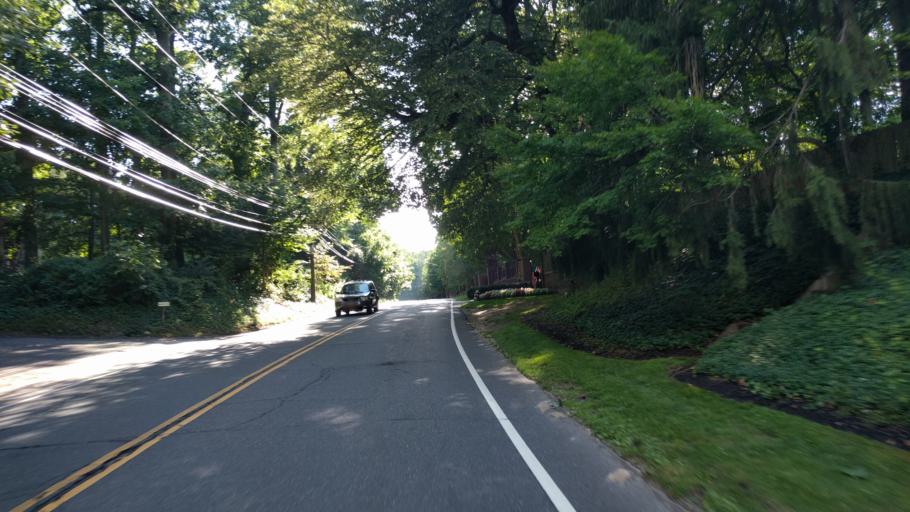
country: US
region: New York
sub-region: Nassau County
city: Oyster Bay Cove
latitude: 40.8717
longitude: -73.5177
